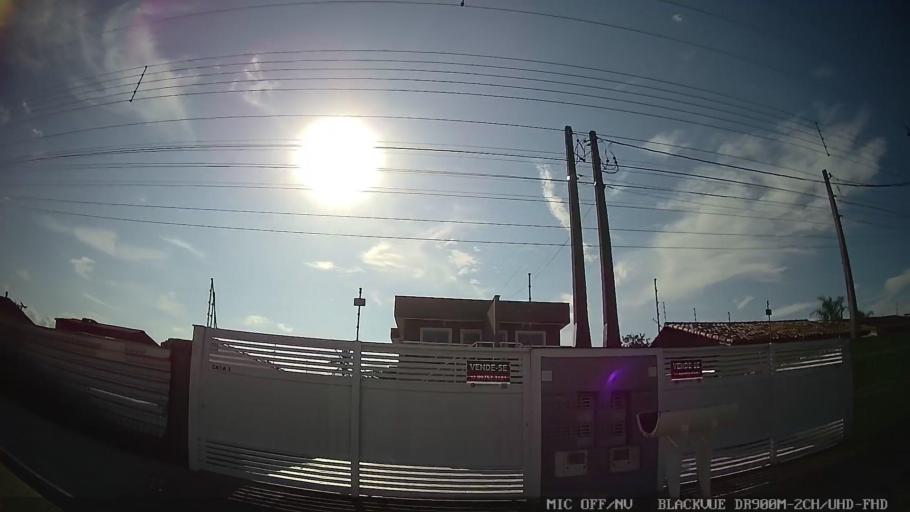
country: BR
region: Sao Paulo
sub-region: Itanhaem
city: Itanhaem
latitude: -24.1768
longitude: -46.8146
